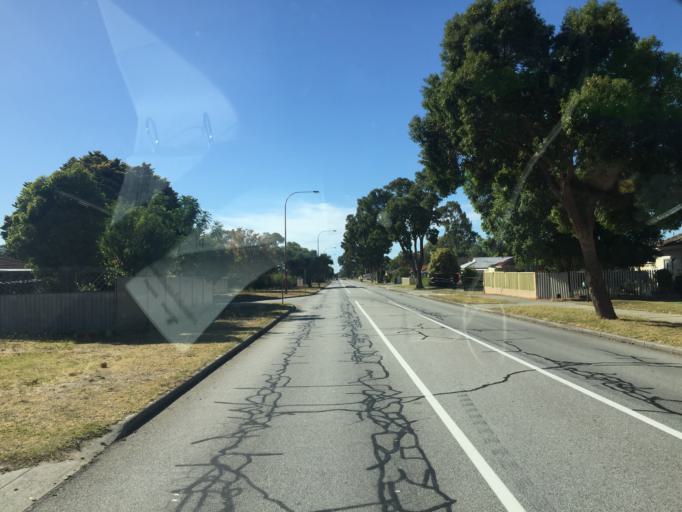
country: AU
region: Western Australia
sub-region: Gosnells
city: Gosnells
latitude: -32.0592
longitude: 116.0070
